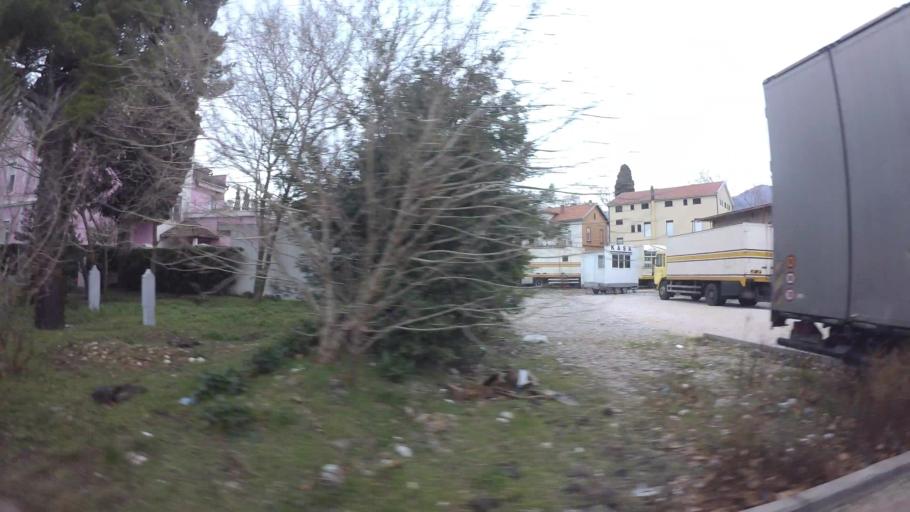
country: BA
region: Federation of Bosnia and Herzegovina
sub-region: Hercegovacko-Bosanski Kanton
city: Mostar
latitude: 43.3417
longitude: 17.8052
